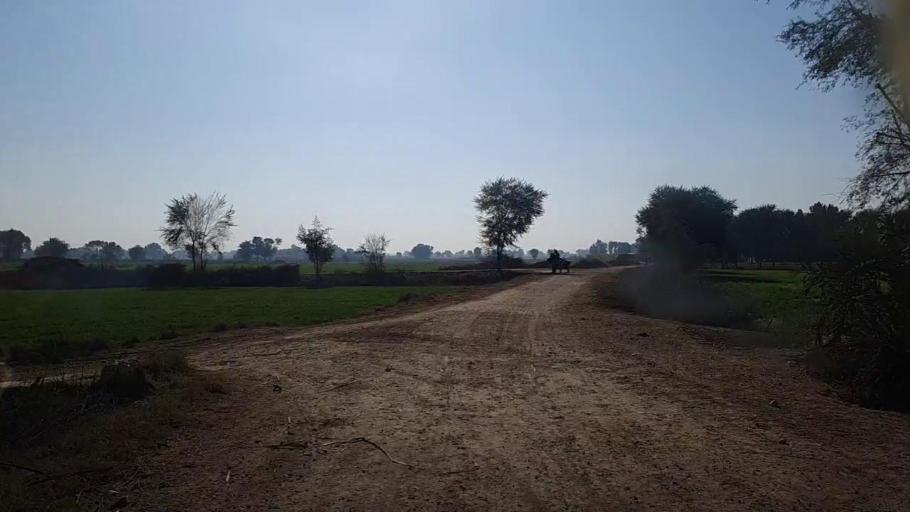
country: PK
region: Sindh
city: Khairpur
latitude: 28.0551
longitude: 69.7482
